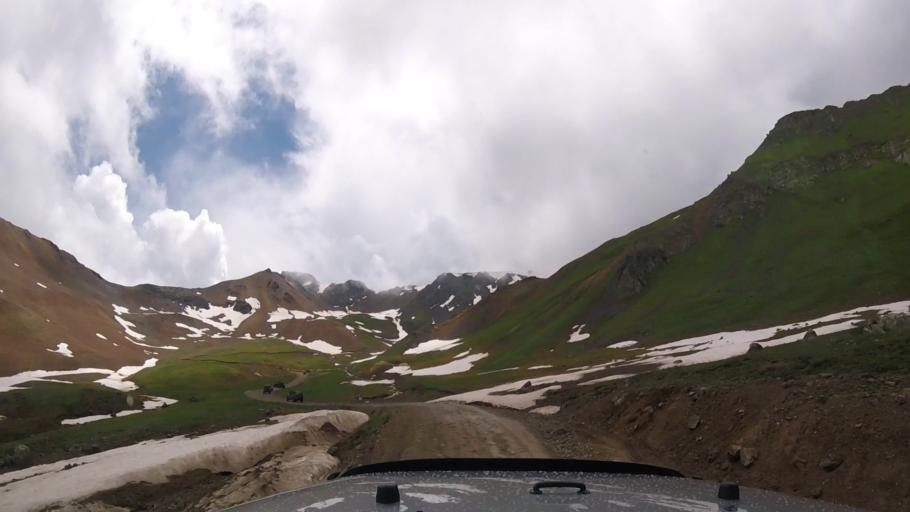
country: US
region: Colorado
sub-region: San Juan County
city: Silverton
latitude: 37.9190
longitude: -107.6126
